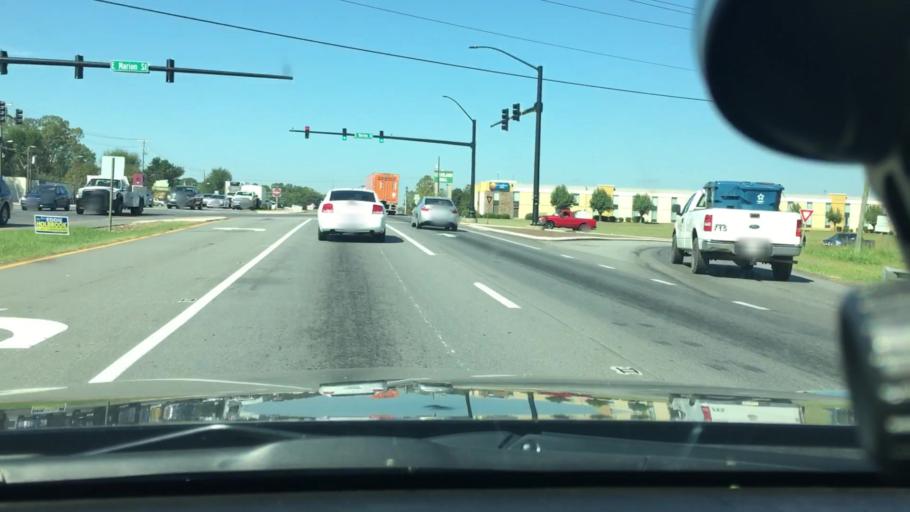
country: US
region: North Carolina
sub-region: Cleveland County
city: Shelby
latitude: 35.2657
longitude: -81.4785
